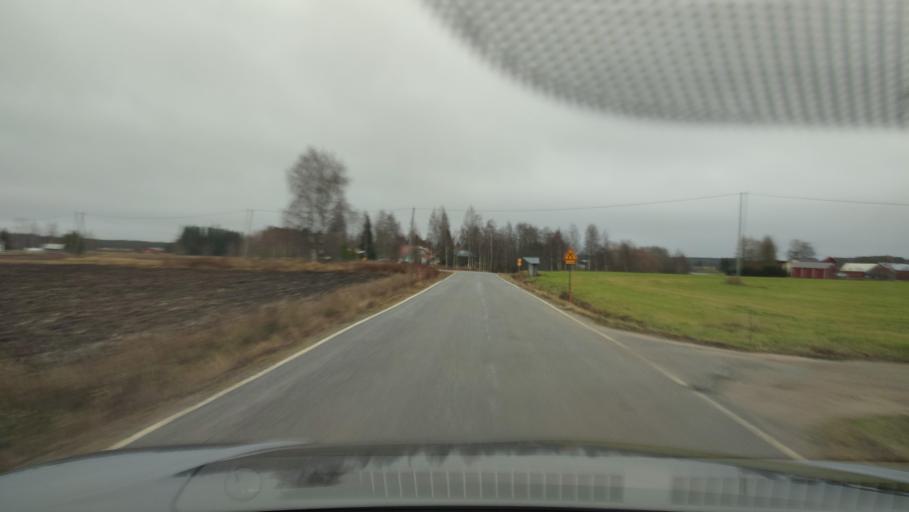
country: FI
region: Southern Ostrobothnia
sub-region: Suupohja
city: Isojoki
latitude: 62.1925
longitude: 21.9617
